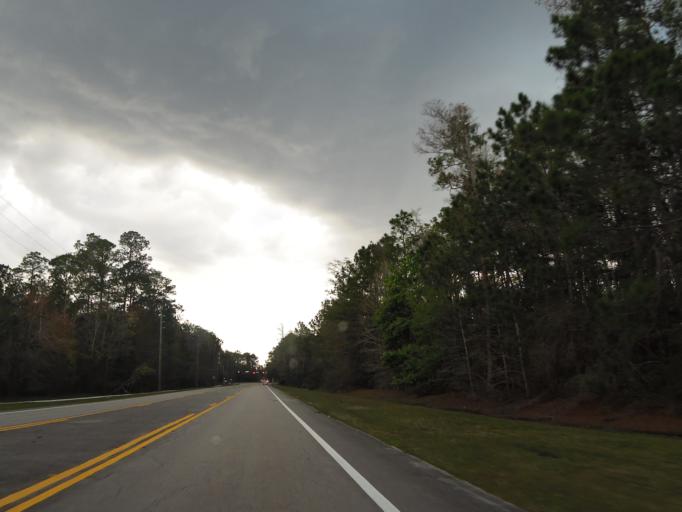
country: US
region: Florida
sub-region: Saint Johns County
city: Fruit Cove
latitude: 30.1898
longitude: -81.5799
